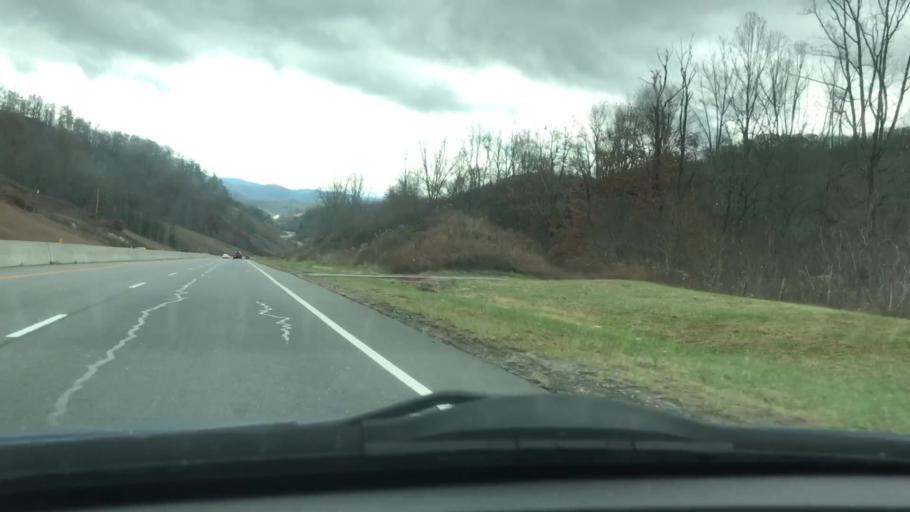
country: US
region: North Carolina
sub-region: Madison County
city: Mars Hill
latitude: 35.8983
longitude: -82.4726
